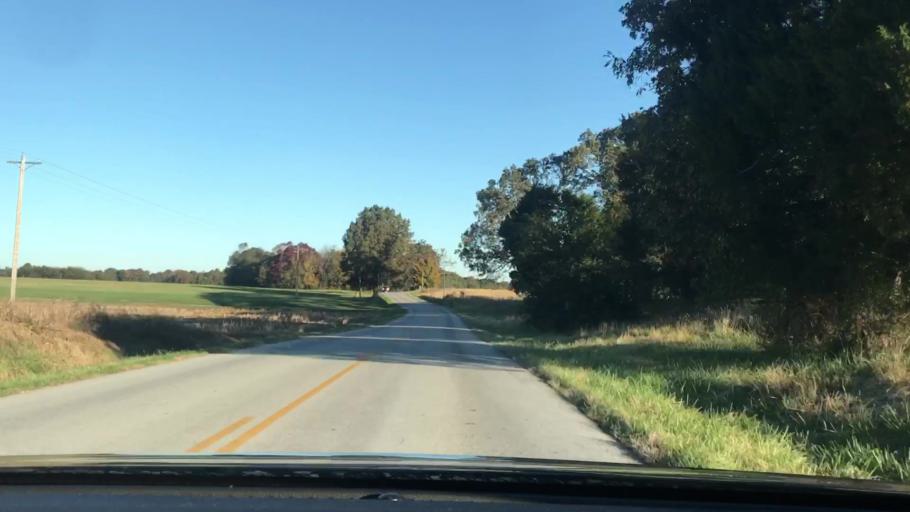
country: US
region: Kentucky
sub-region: Simpson County
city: Franklin
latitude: 36.7926
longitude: -86.6273
